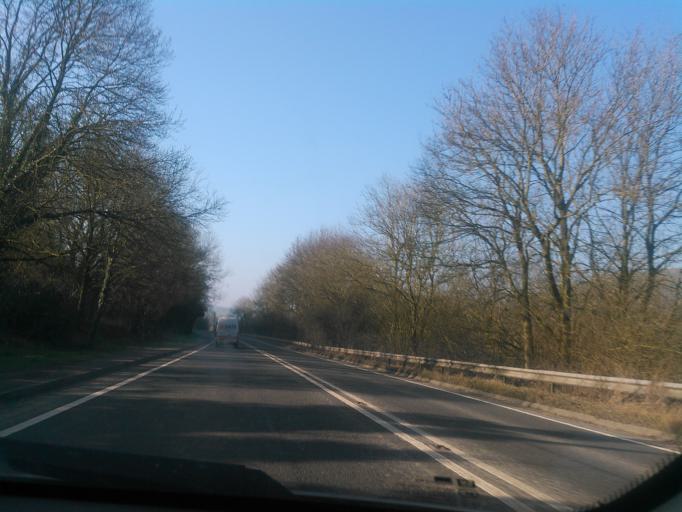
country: GB
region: England
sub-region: Shropshire
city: Church Stretton
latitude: 52.5271
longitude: -2.8134
